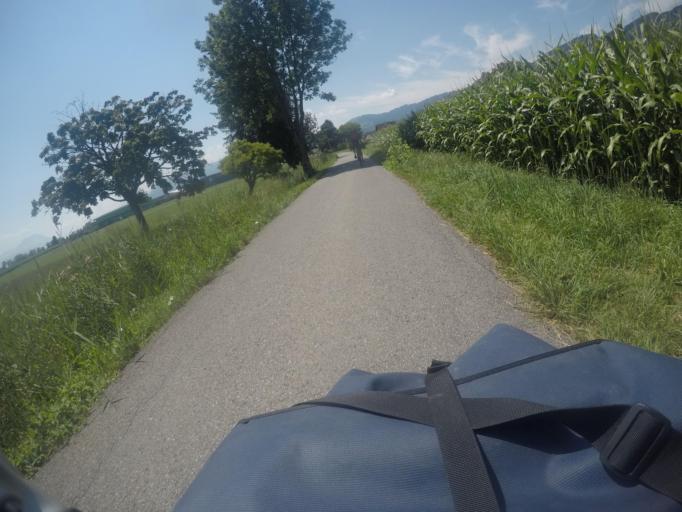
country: CH
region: Saint Gallen
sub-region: Wahlkreis Rheintal
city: Rebstein
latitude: 47.3996
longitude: 9.5958
